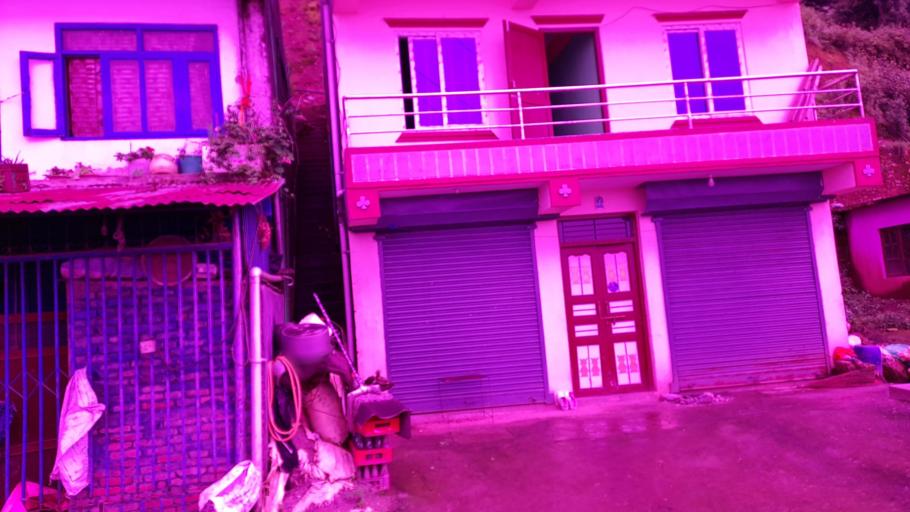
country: NP
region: Central Region
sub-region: Bagmati Zone
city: Kathmandu
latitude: 27.8311
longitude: 85.2371
